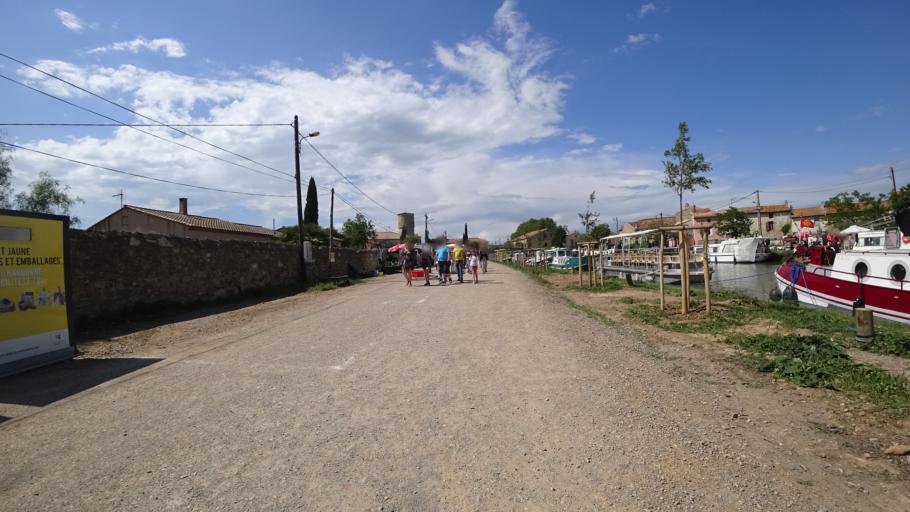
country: FR
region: Languedoc-Roussillon
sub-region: Departement de l'Aude
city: Saint-Marcel-sur-Aude
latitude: 43.2649
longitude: 2.9045
